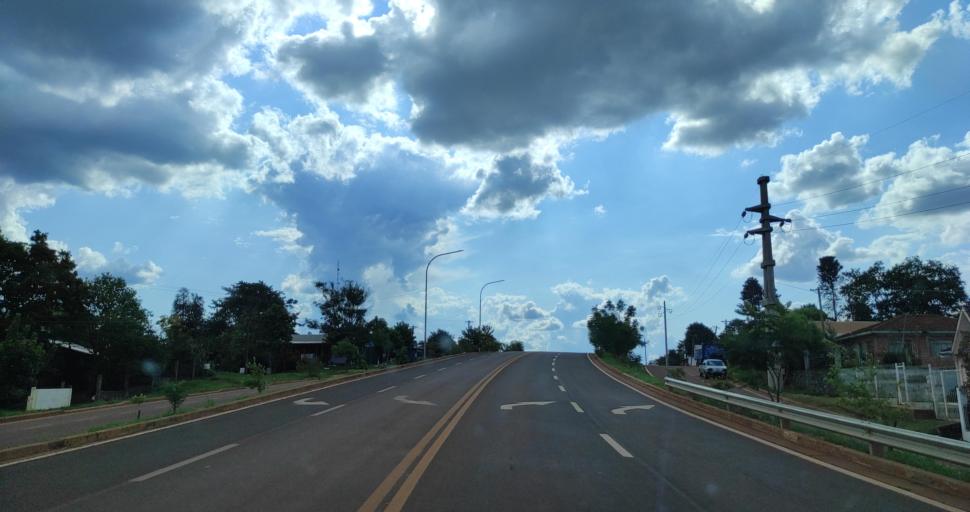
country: AR
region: Misiones
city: Bernardo de Irigoyen
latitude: -26.2956
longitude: -53.7501
